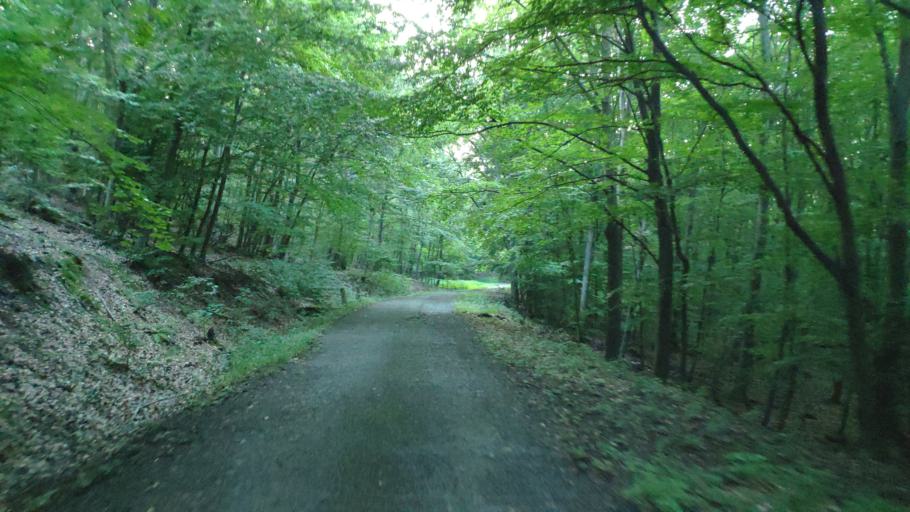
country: SK
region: Kosicky
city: Secovce
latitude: 48.5855
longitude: 21.5315
